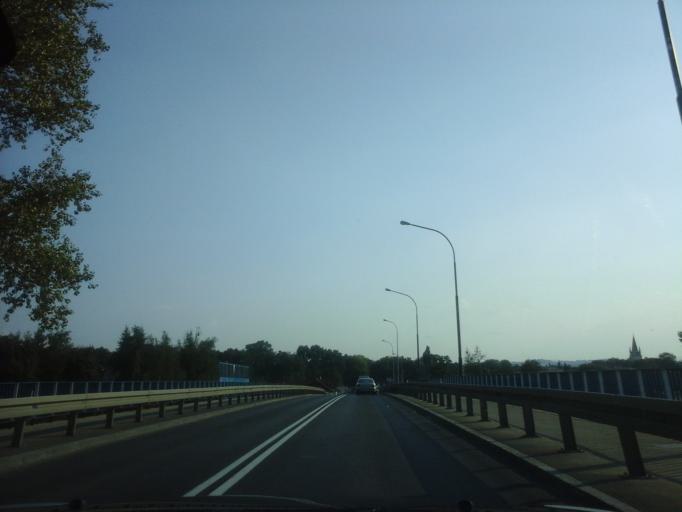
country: PL
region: Lesser Poland Voivodeship
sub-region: Powiat krakowski
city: Skawina
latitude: 49.9799
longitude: 19.8353
